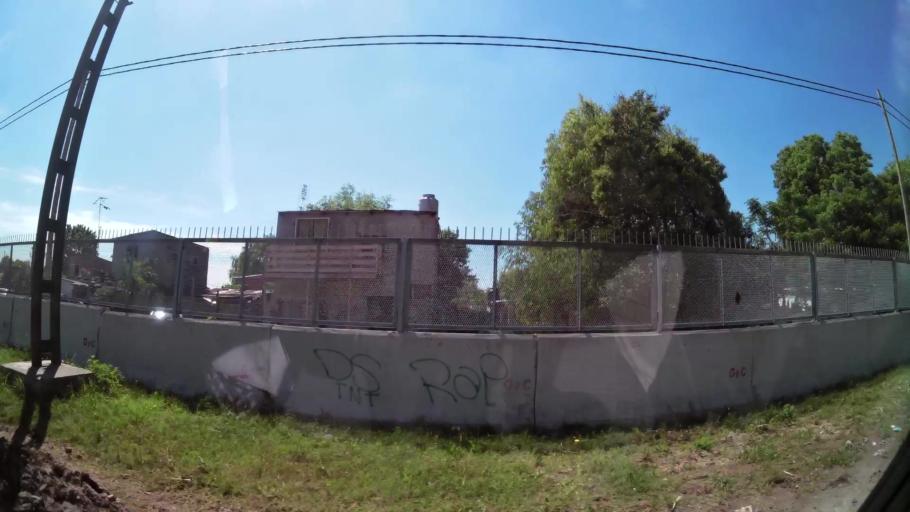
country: AR
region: Buenos Aires
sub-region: Partido de Tigre
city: Tigre
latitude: -34.4292
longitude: -58.5623
